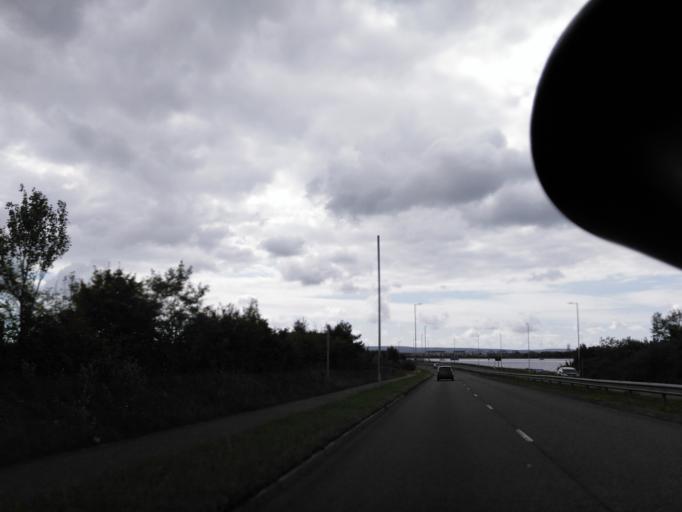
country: GB
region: England
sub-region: Poole
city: Poole
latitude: 50.7274
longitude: -1.9919
